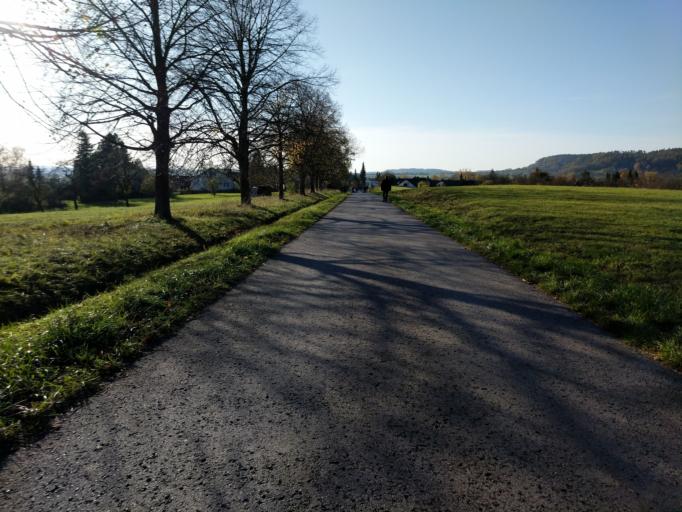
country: DE
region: Baden-Wuerttemberg
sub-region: Tuebingen Region
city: Rottenburg
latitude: 48.5084
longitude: 8.9763
